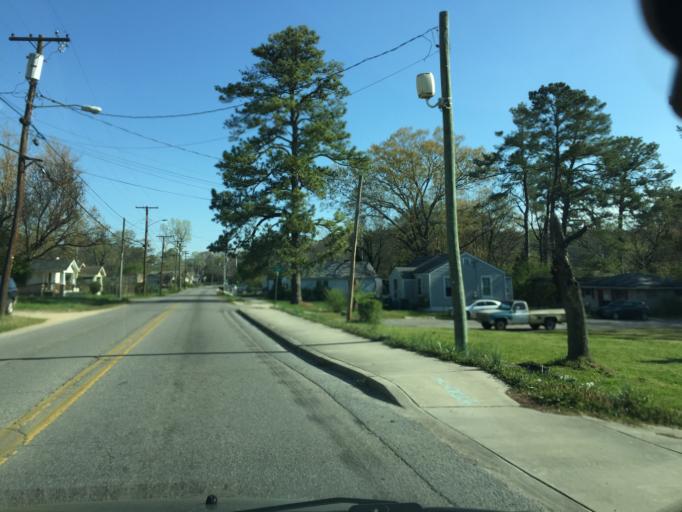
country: US
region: Tennessee
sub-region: Hamilton County
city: East Chattanooga
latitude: 35.0408
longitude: -85.2393
